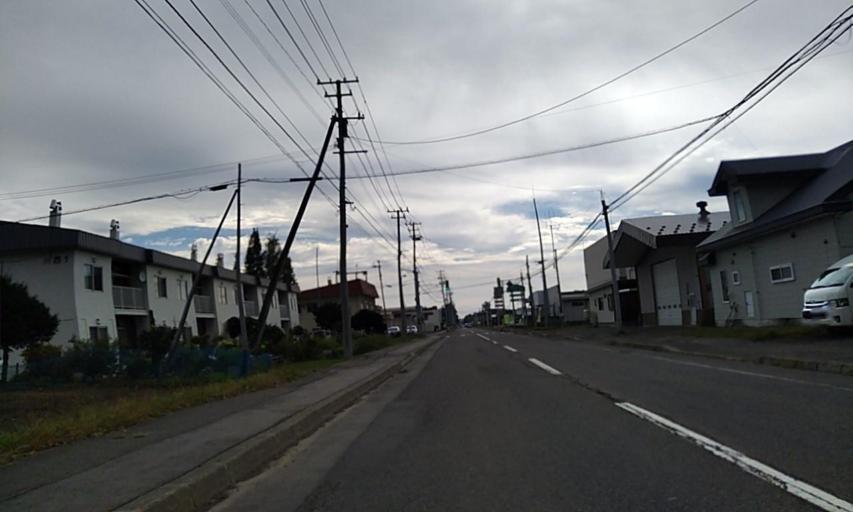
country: JP
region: Hokkaido
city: Obihiro
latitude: 42.8504
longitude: 143.1635
